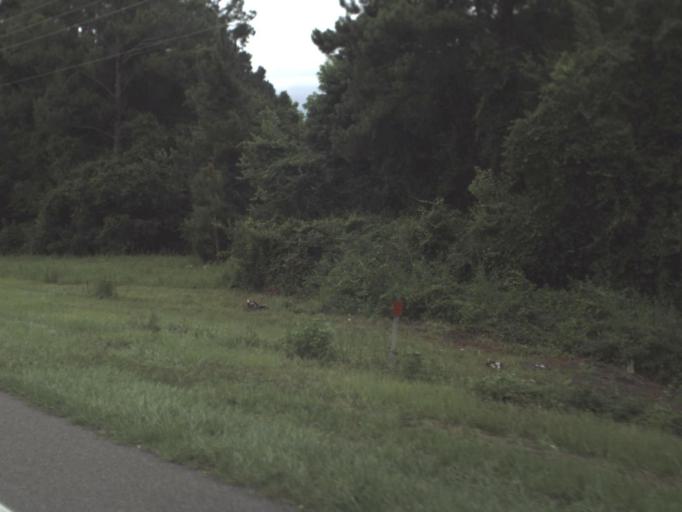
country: US
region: Florida
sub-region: Clay County
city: Keystone Heights
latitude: 29.8494
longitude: -82.0690
